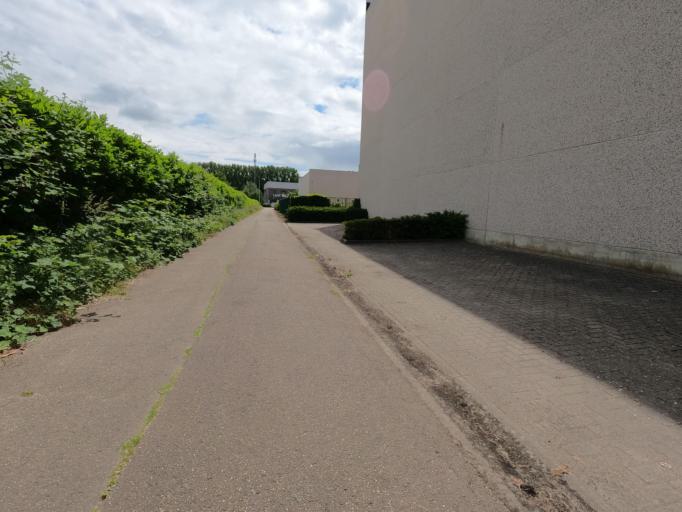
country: BE
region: Flanders
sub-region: Provincie Vlaams-Brabant
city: Holsbeek
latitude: 50.9417
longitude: 4.7495
